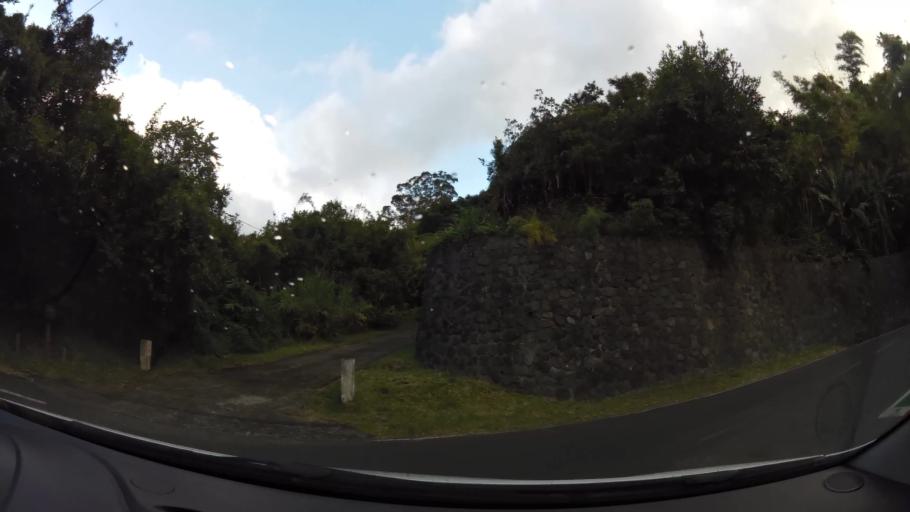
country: RE
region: Reunion
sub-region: Reunion
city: Saint-Denis
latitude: -20.9185
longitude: 55.4389
